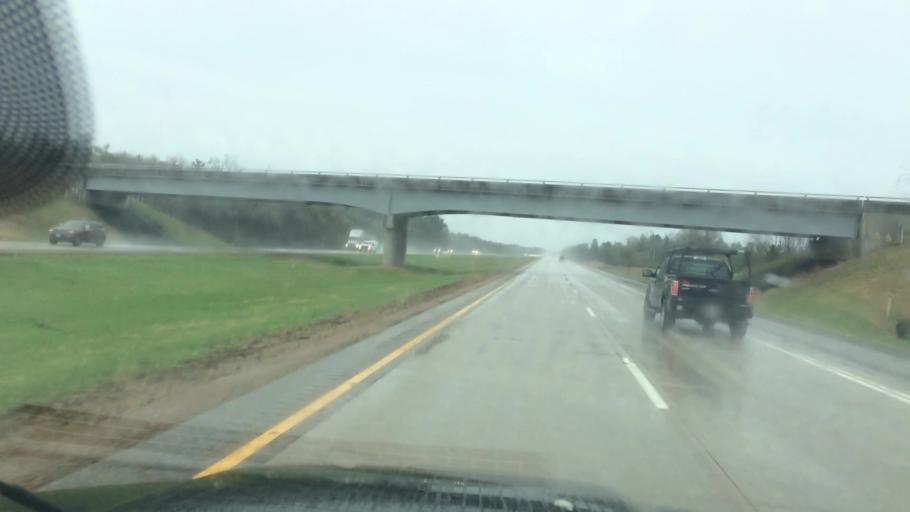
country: US
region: Wisconsin
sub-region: Portage County
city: Stevens Point
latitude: 44.6282
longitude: -89.6333
